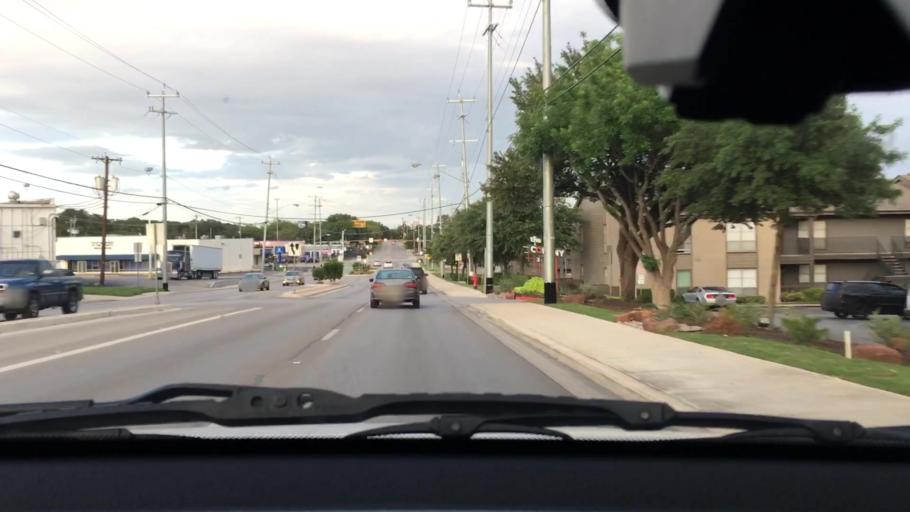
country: US
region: Texas
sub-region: Bexar County
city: Universal City
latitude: 29.5509
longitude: -98.3068
